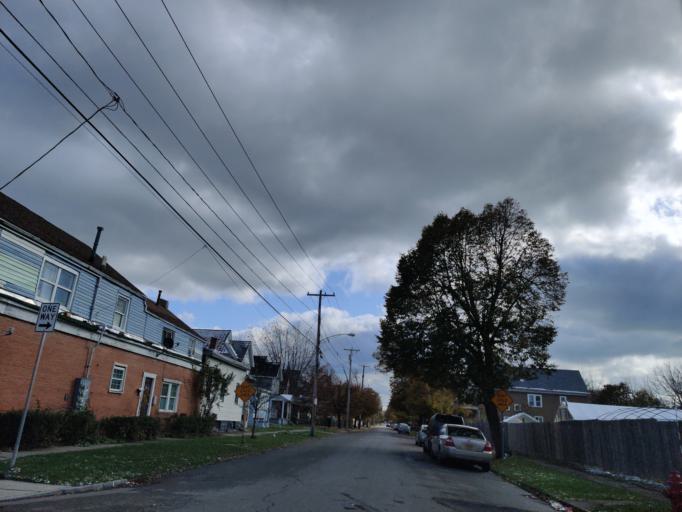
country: US
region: New York
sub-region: Erie County
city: Buffalo
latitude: 42.9074
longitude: -78.8894
